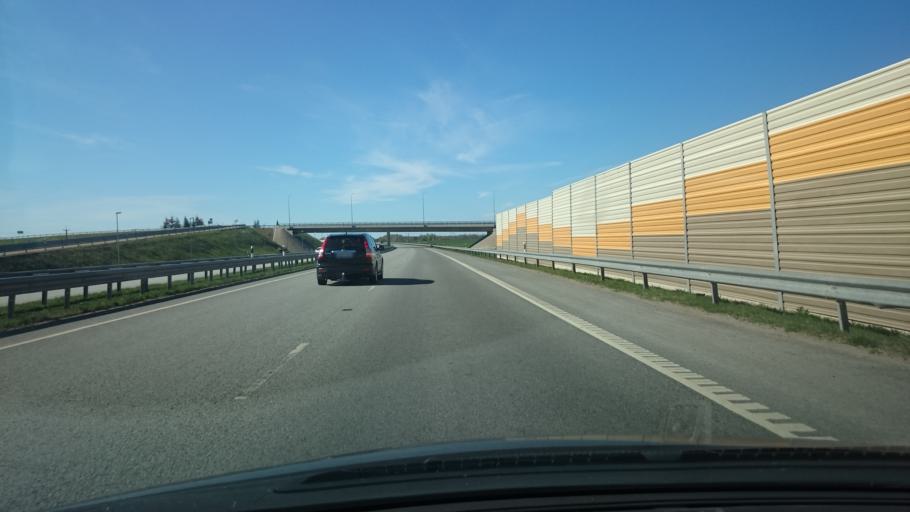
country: EE
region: Ida-Virumaa
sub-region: Johvi vald
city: Johvi
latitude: 59.3736
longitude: 27.3814
